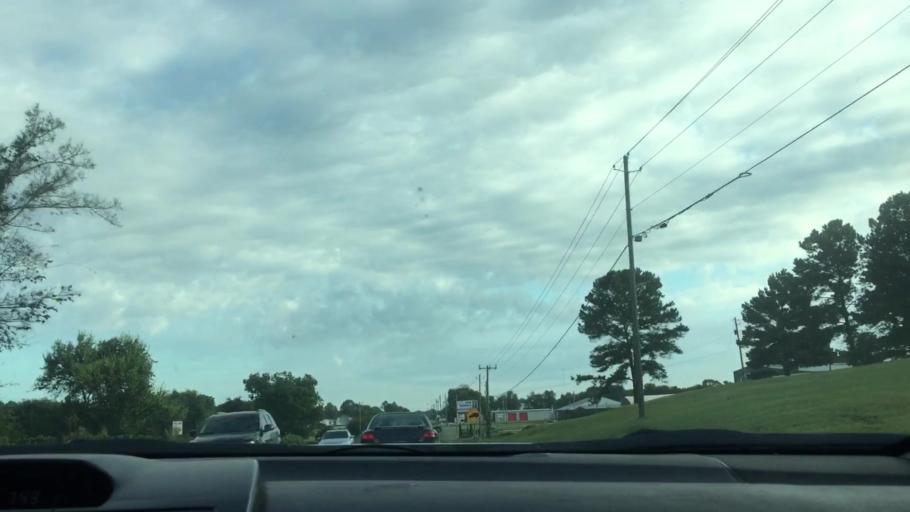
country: US
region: Alabama
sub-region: Hale County
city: Moundville
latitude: 32.9802
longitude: -87.6246
